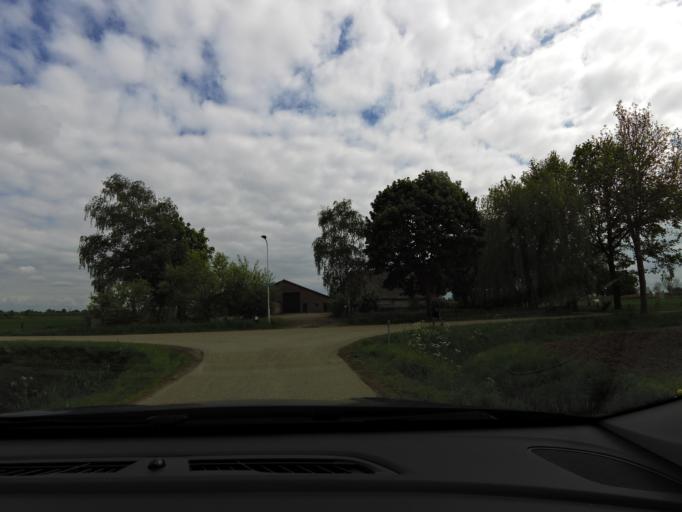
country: NL
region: Gelderland
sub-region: Gemeente Tiel
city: Tiel
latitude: 51.9310
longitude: 5.4622
